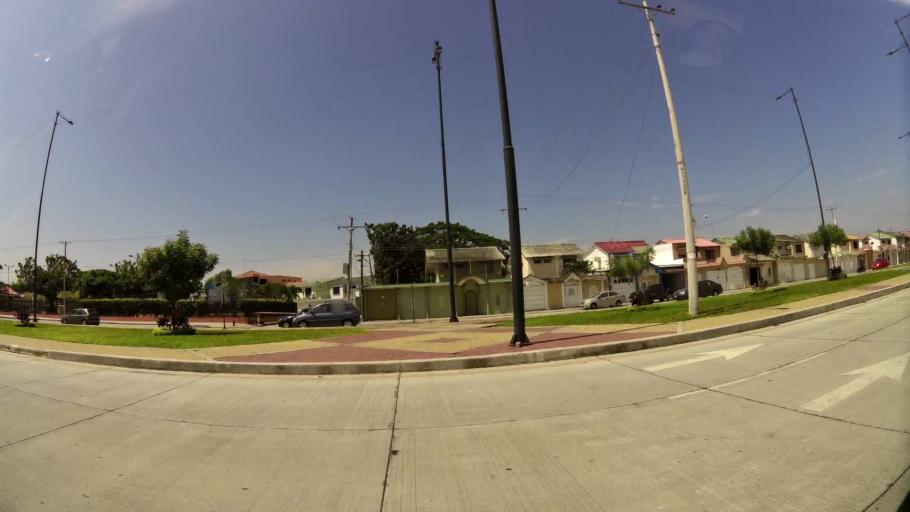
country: EC
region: Guayas
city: Eloy Alfaro
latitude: -2.1101
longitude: -79.8990
